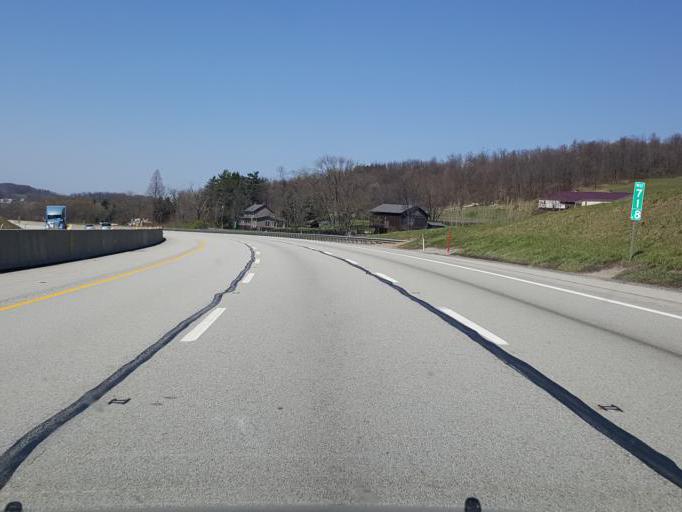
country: US
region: Pennsylvania
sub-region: Westmoreland County
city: New Stanton
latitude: 40.2599
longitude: -79.6440
